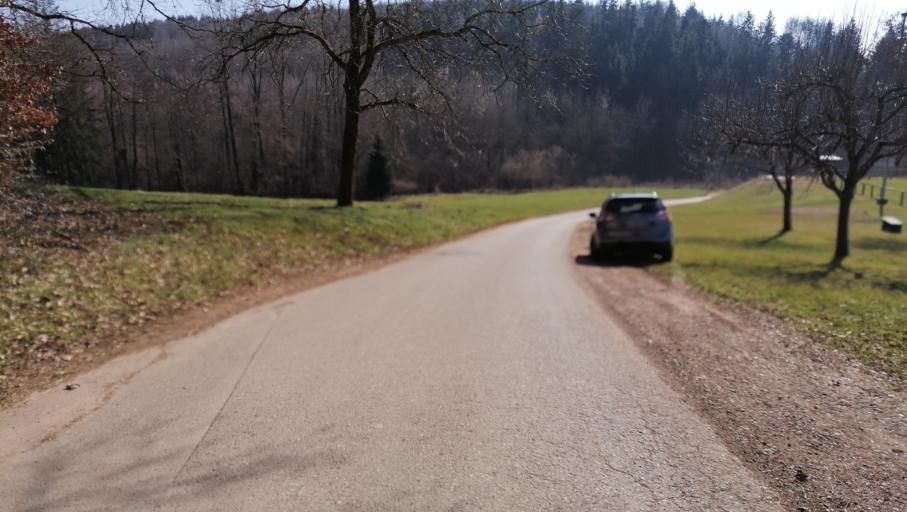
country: CH
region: Aargau
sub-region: Bezirk Rheinfelden
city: Mumpf
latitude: 47.5823
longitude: 7.9202
